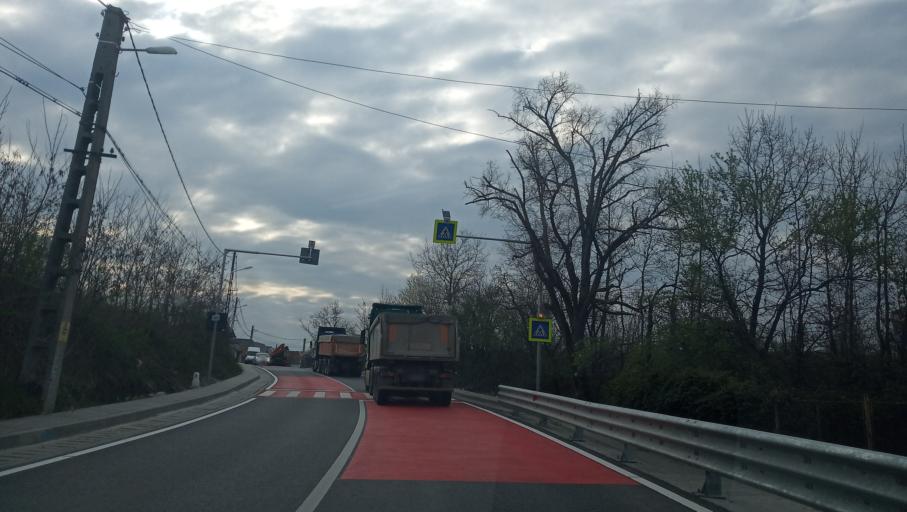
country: RO
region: Bihor
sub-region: Comuna Rieni
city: Ghighiseni
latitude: 46.5531
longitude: 22.4469
